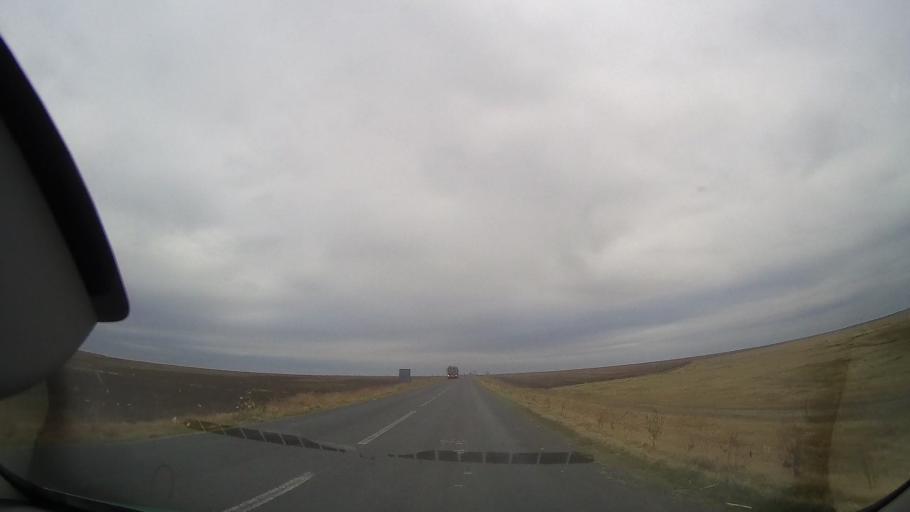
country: RO
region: Buzau
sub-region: Comuna Padina
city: Padina
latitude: 44.8154
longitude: 27.1230
